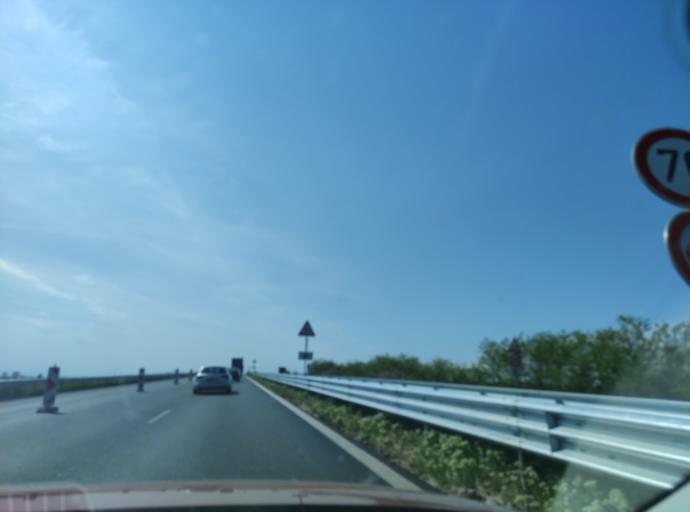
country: BG
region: Plovdiv
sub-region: Obshtina Brezovo
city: Brezovo
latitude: 42.1965
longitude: 25.1365
